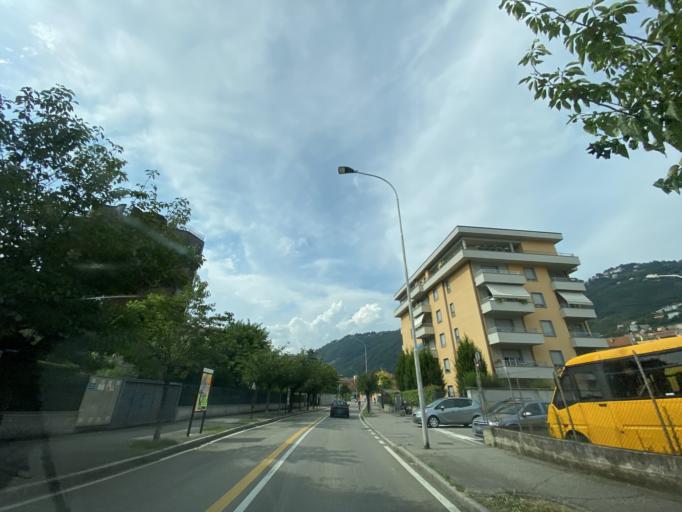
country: IT
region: Lombardy
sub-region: Provincia di Como
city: Como
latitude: 45.8038
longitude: 9.0909
